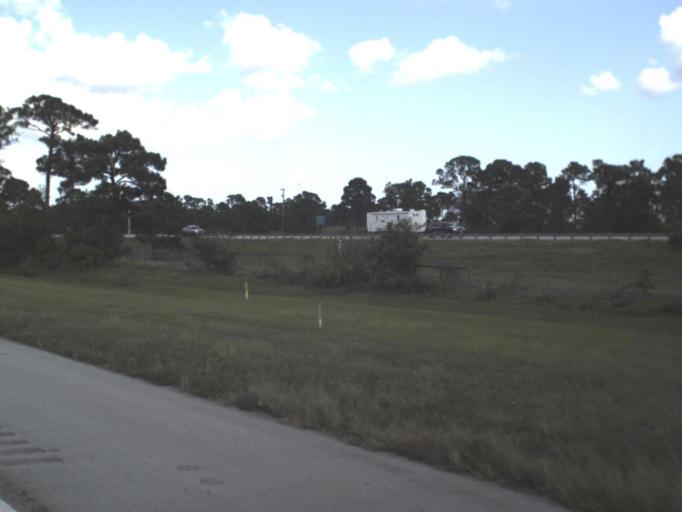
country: US
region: Florida
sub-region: Palm Beach County
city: Limestone Creek
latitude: 26.9726
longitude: -80.1787
